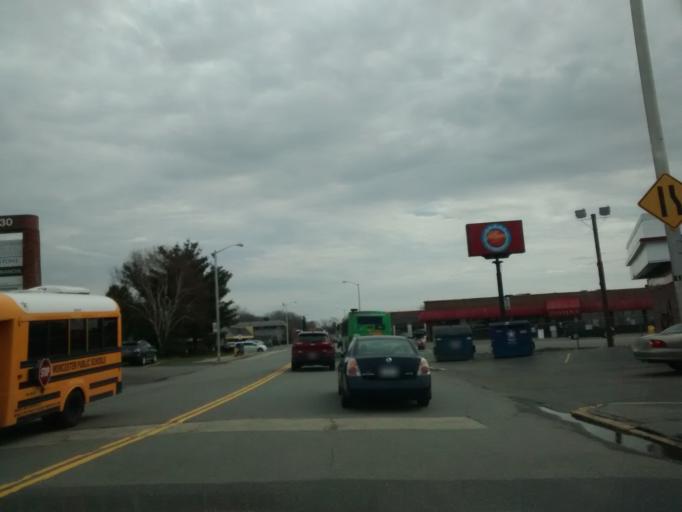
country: US
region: Massachusetts
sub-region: Worcester County
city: Worcester
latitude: 42.2845
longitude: -71.8076
